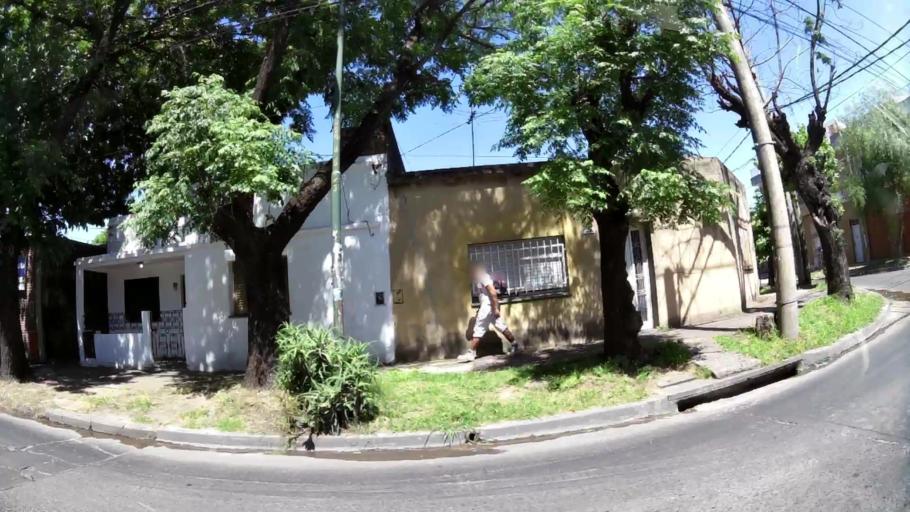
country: AR
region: Buenos Aires
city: Caseros
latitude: -34.5687
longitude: -58.5723
